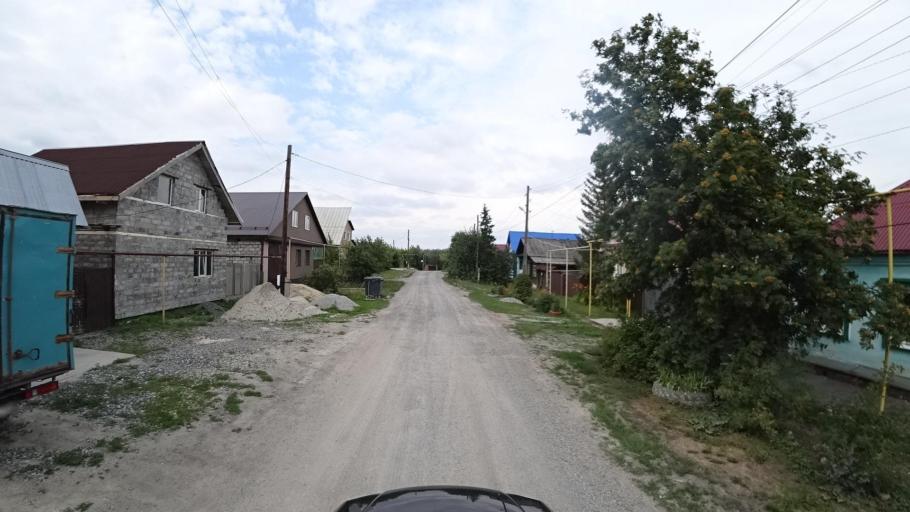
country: RU
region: Sverdlovsk
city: Kamyshlov
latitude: 56.8499
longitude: 62.6958
